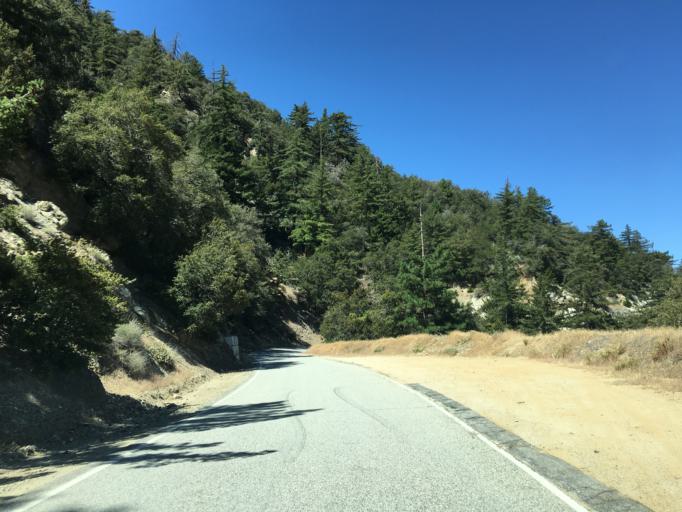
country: US
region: California
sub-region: San Bernardino County
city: San Antonio Heights
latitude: 34.2252
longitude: -117.6787
